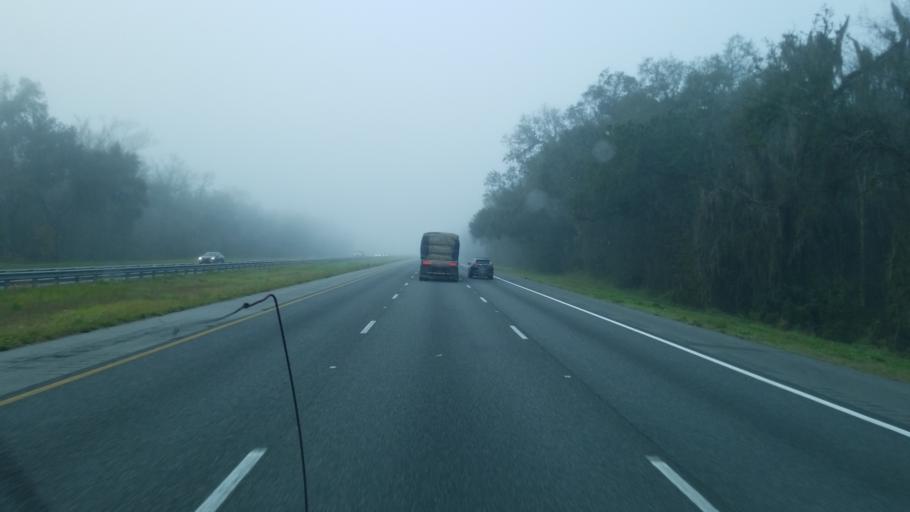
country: US
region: Florida
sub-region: Sumter County
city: Bushnell
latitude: 28.6241
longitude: -82.1791
